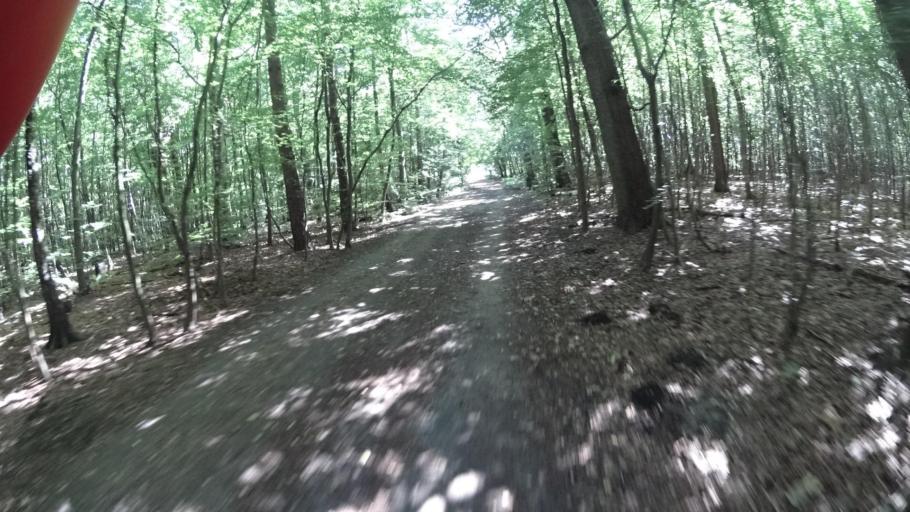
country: PL
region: Masovian Voivodeship
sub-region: Powiat piaseczynski
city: Jozefoslaw
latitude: 52.1104
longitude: 21.0555
